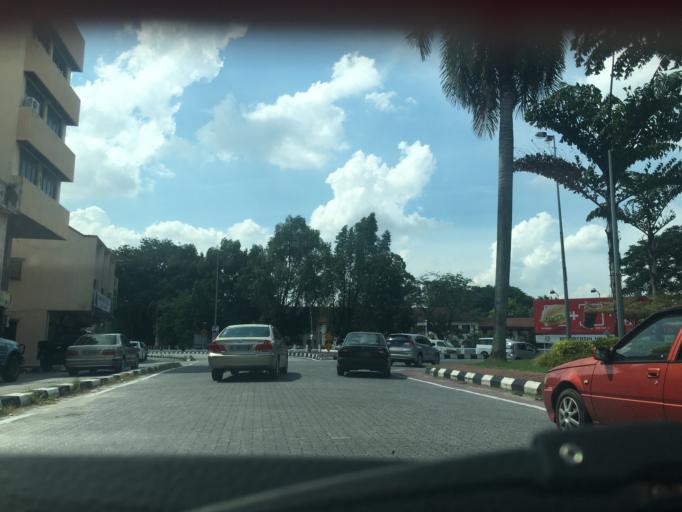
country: MY
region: Perak
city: Ipoh
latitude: 4.5857
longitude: 101.0847
